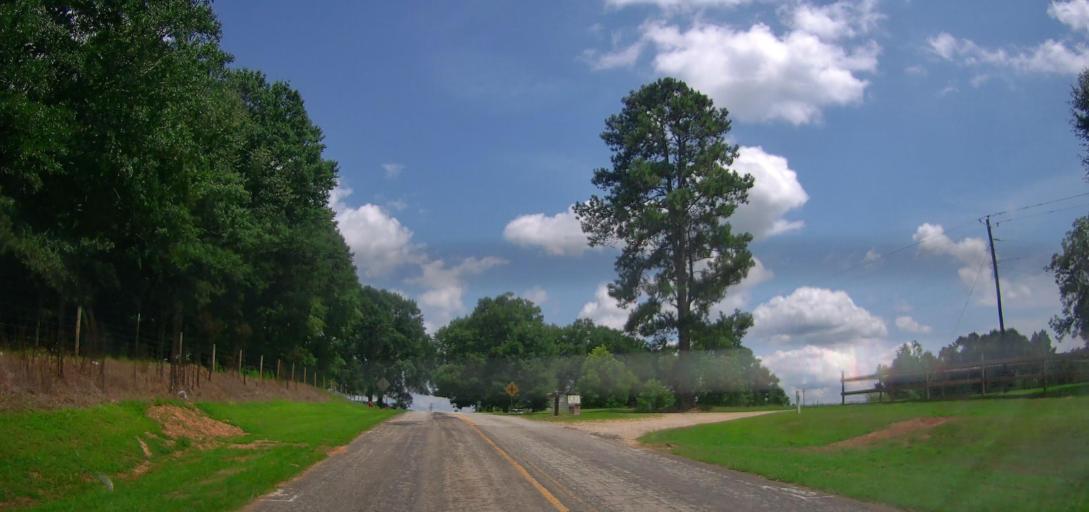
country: US
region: Georgia
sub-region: Carroll County
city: Bowdon
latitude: 33.5064
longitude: -85.3316
